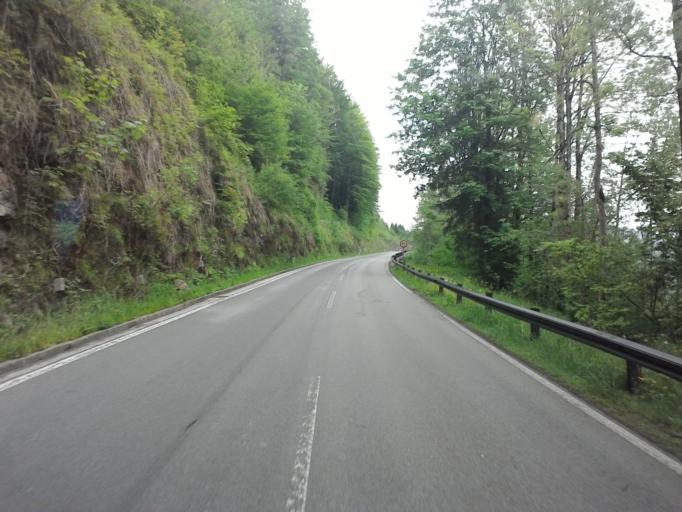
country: AT
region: Styria
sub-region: Politischer Bezirk Liezen
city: Gams bei Hieflau
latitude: 47.6364
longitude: 14.7591
